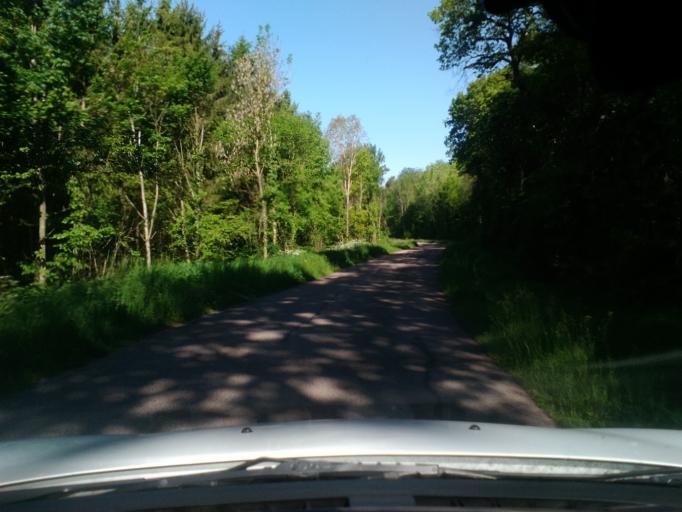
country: FR
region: Lorraine
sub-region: Departement des Vosges
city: Mirecourt
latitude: 48.3084
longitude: 6.1769
